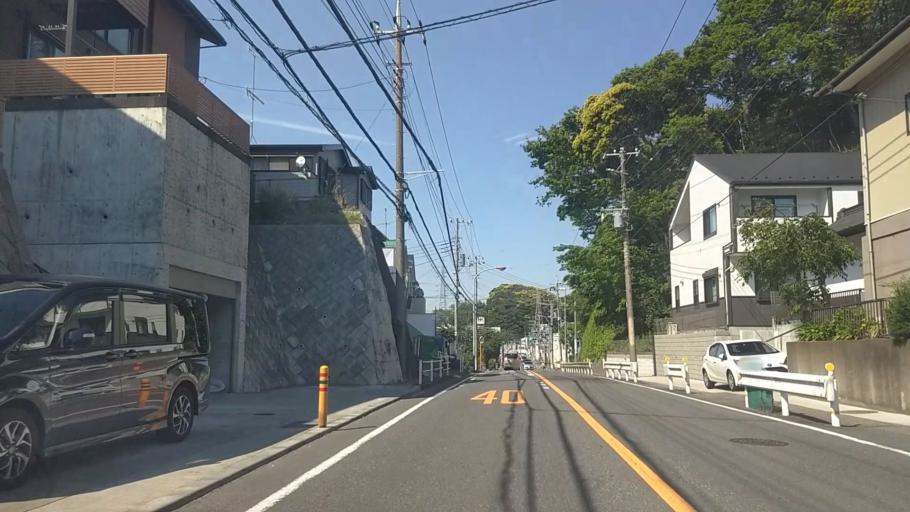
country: JP
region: Kanagawa
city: Kamakura
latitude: 35.3526
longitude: 139.5429
